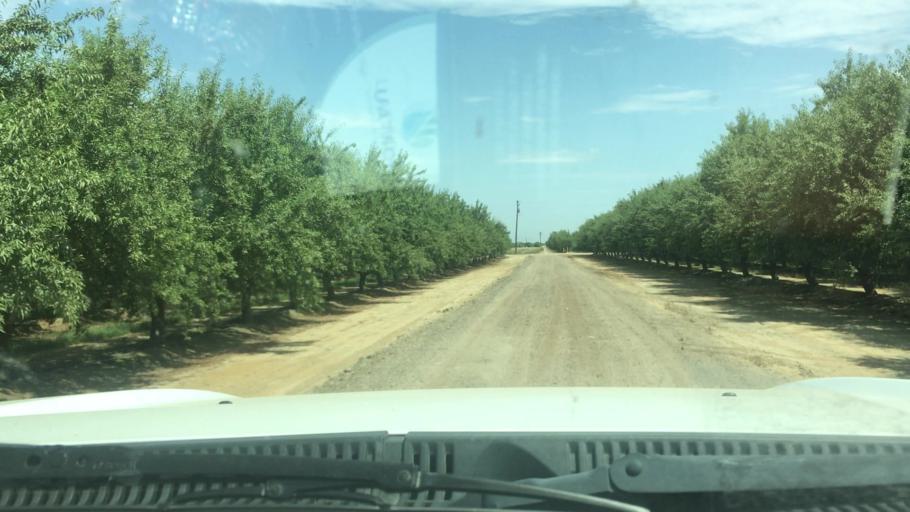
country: US
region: California
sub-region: Kern County
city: Wasco
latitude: 35.5561
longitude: -119.4296
